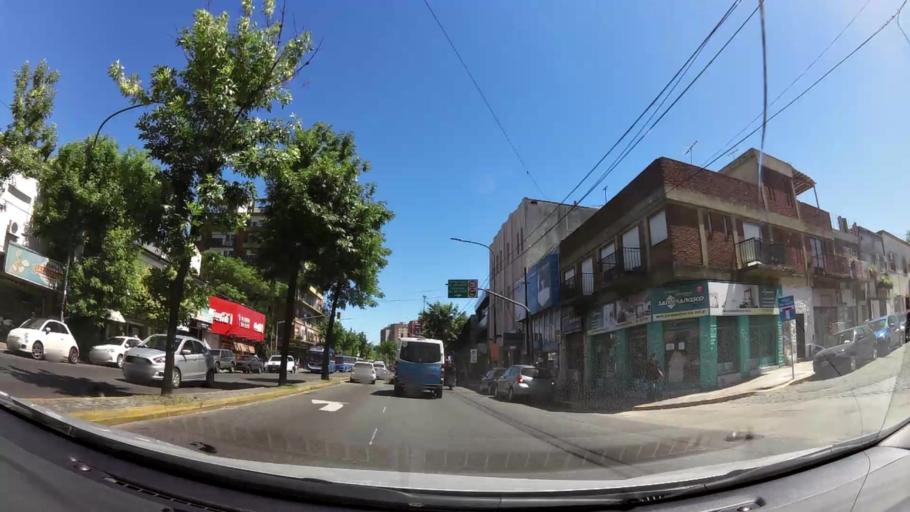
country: AR
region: Buenos Aires
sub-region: Partido de San Isidro
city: San Isidro
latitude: -34.4700
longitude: -58.5166
